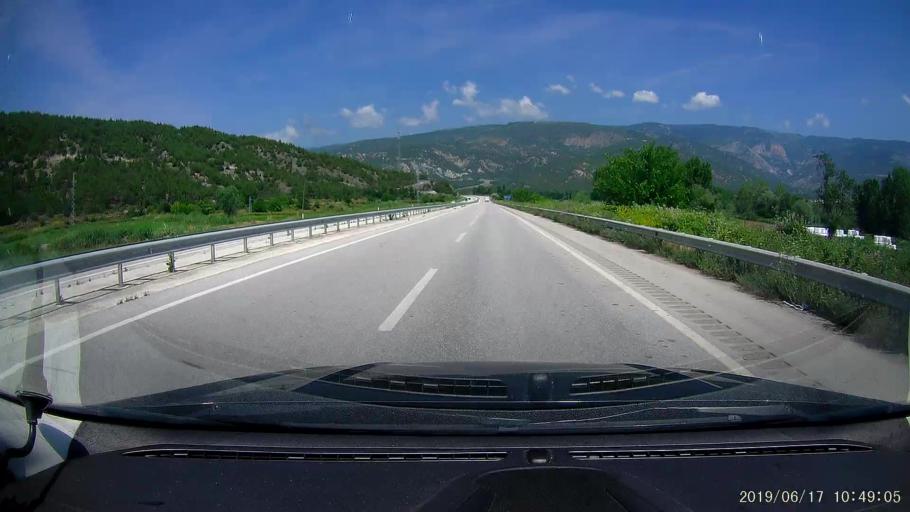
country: TR
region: Corum
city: Hacihamza
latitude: 41.0973
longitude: 34.4175
